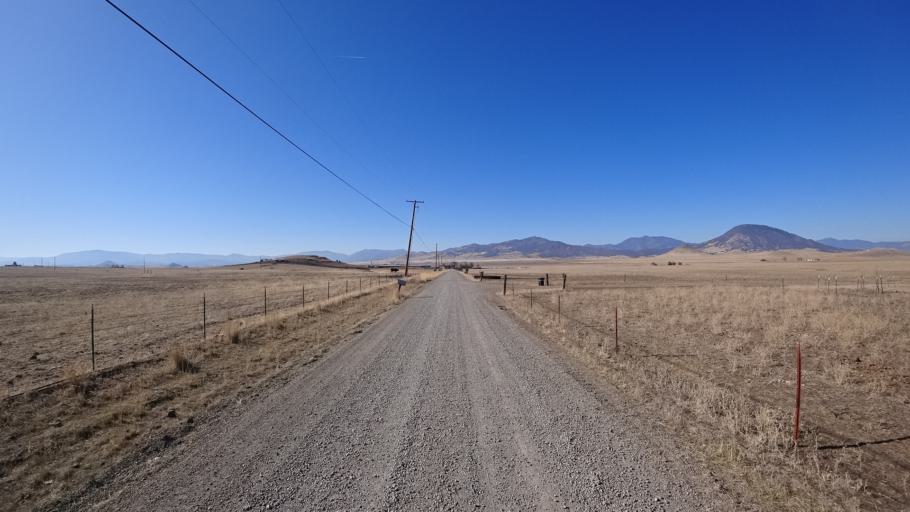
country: US
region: California
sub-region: Siskiyou County
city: Montague
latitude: 41.7939
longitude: -122.4224
